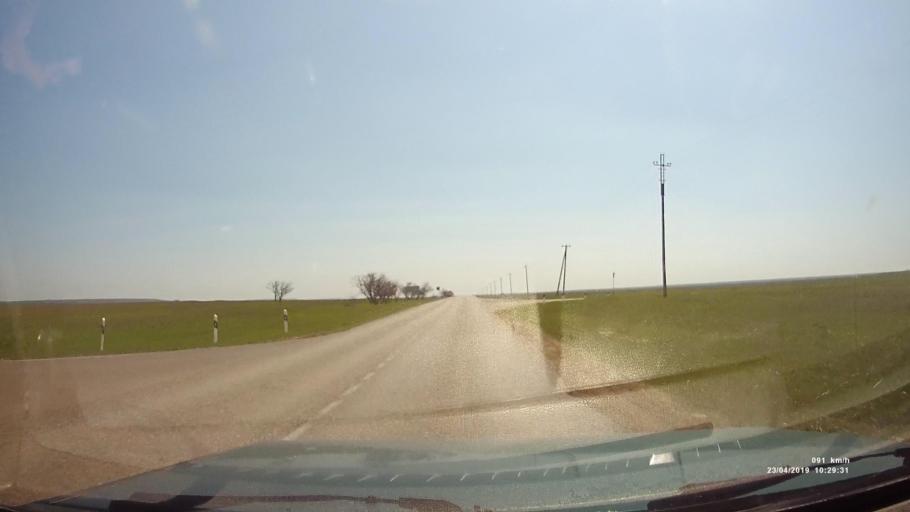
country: RU
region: Kalmykiya
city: Yashalta
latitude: 46.5980
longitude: 42.5278
